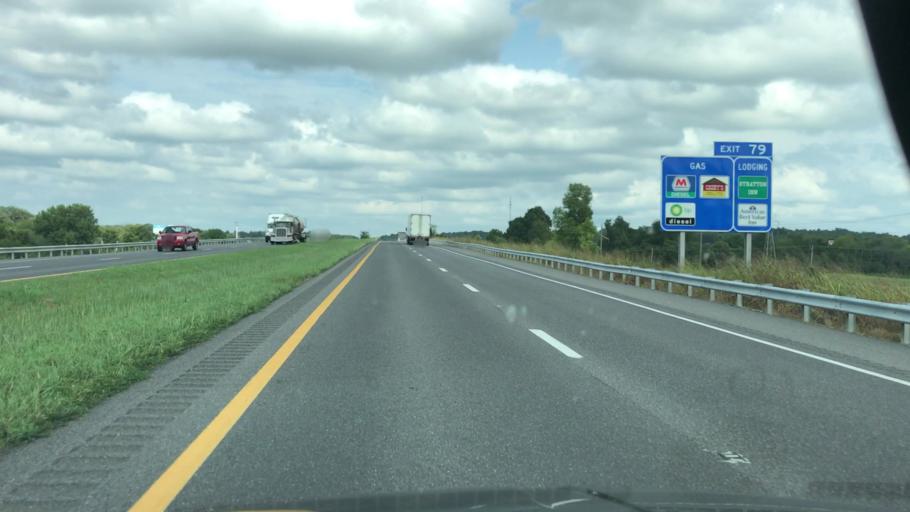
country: US
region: Kentucky
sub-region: Caldwell County
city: Princeton
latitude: 37.1206
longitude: -87.9027
